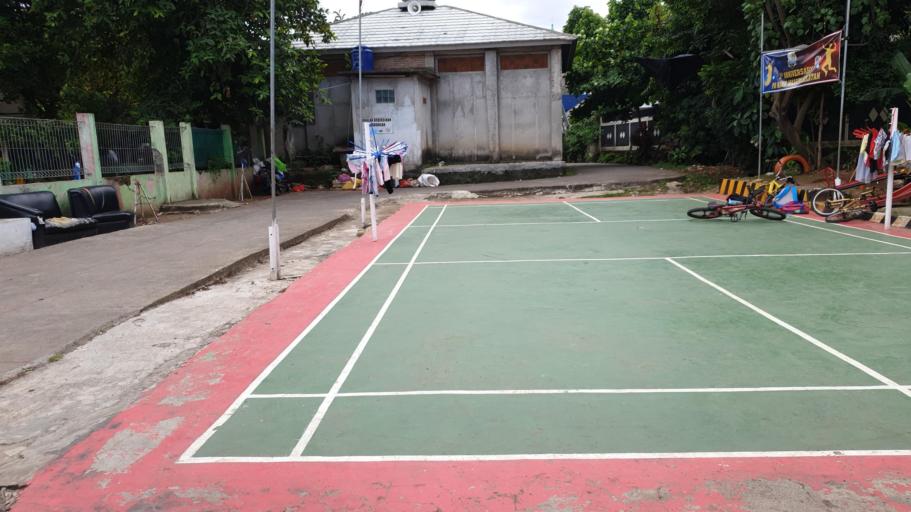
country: ID
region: Jakarta Raya
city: Jakarta
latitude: -6.2659
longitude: 106.7905
